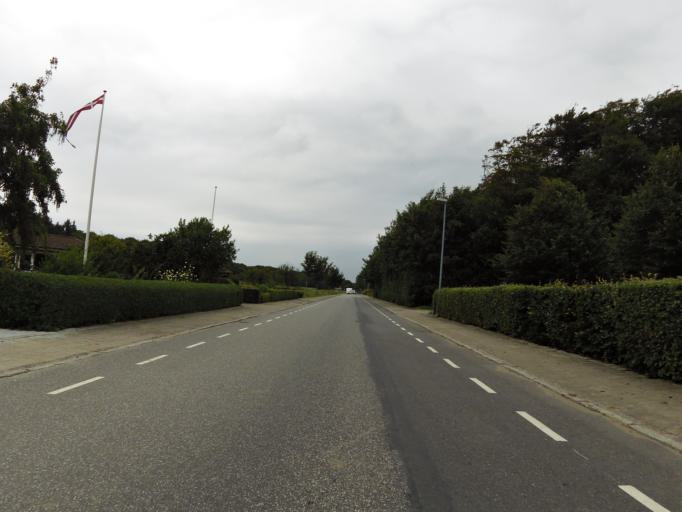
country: DK
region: South Denmark
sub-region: Tonder Kommune
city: Logumkloster
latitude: 55.0802
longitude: 8.9317
